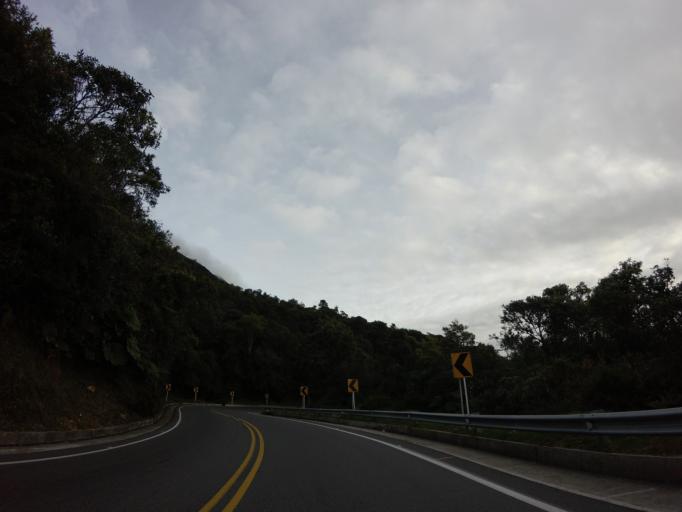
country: CO
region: Tolima
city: Herveo
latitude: 5.0920
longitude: -75.2780
